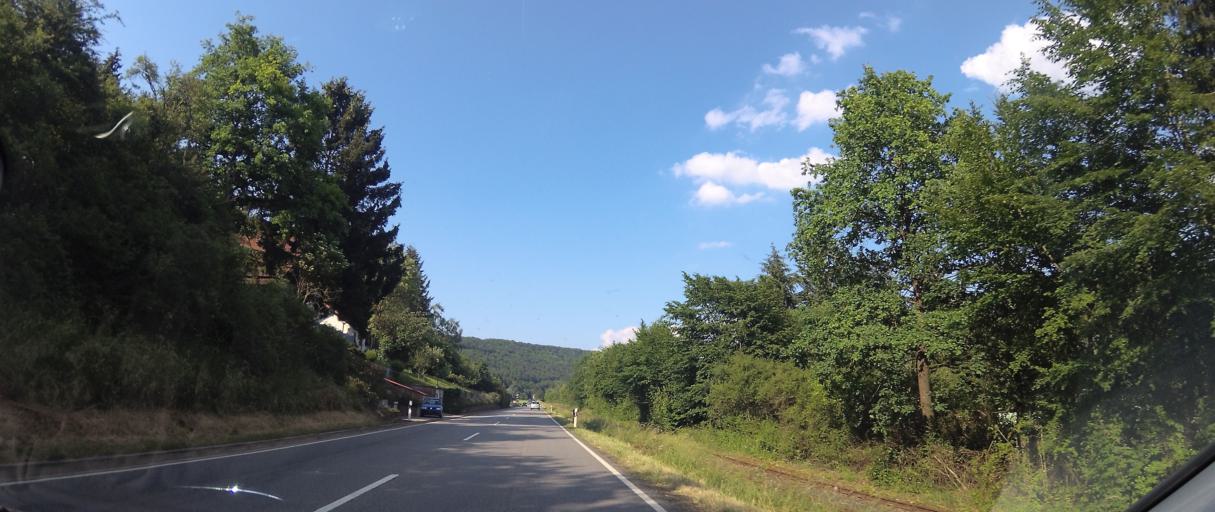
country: DE
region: Rheinland-Pfalz
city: Medard
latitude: 49.6715
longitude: 7.6189
